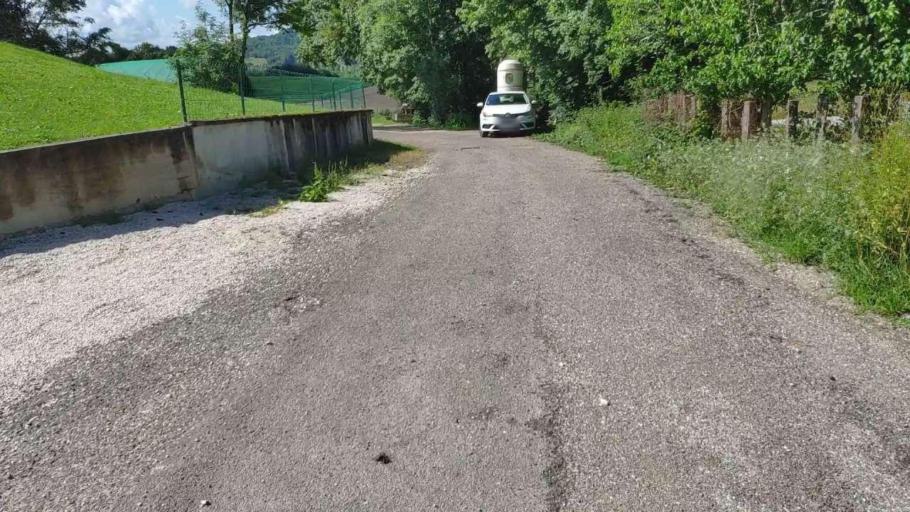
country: FR
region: Franche-Comte
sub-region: Departement du Jura
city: Poligny
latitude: 46.8214
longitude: 5.5848
